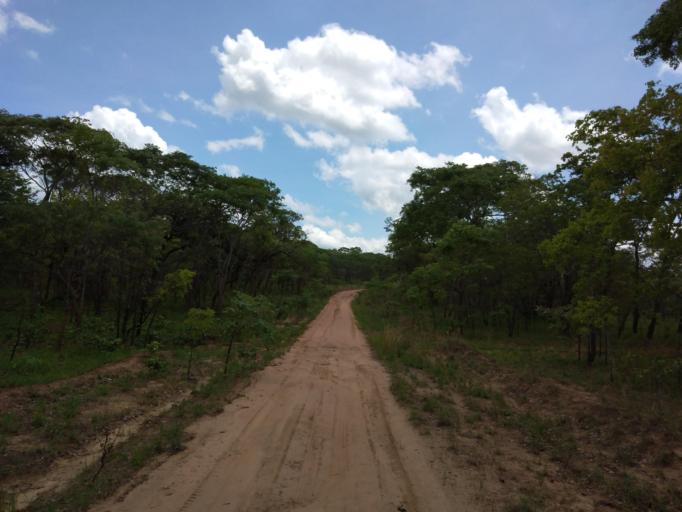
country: ZM
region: Central
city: Mkushi
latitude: -14.0519
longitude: 29.9630
